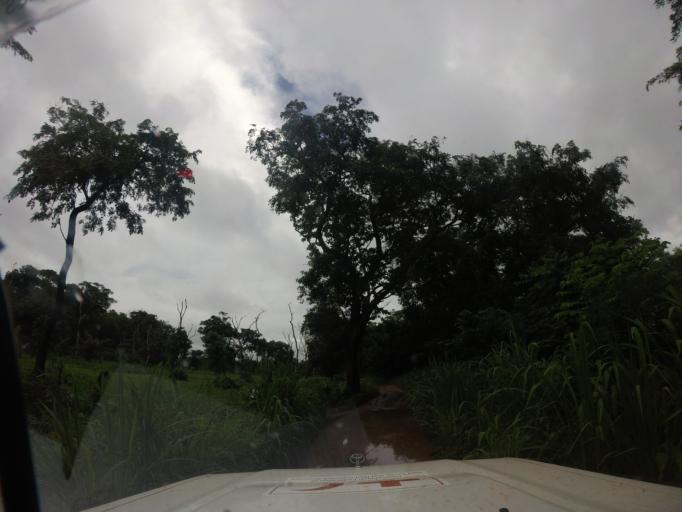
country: SL
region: Northern Province
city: Kamakwie
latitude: 9.6567
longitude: -12.2206
